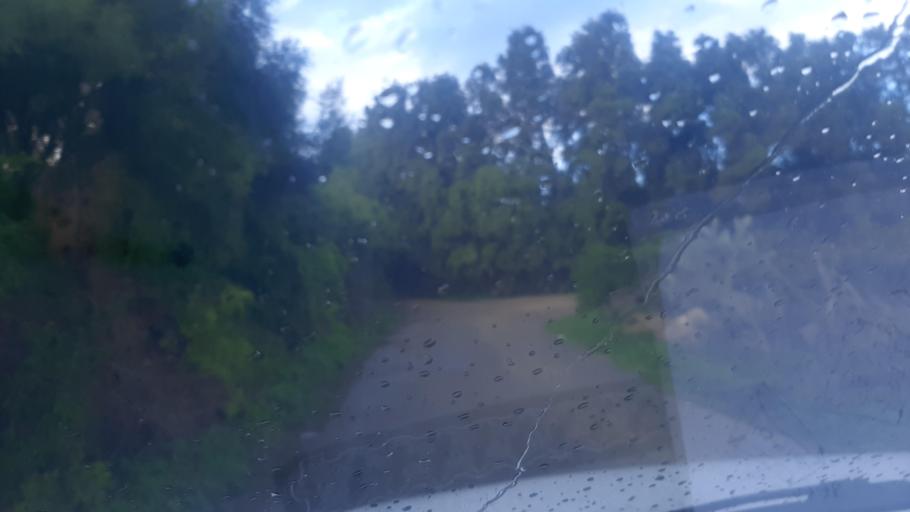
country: TN
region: Nabul
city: Manzil Bu Zalafah
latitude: 36.7371
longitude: 10.5295
